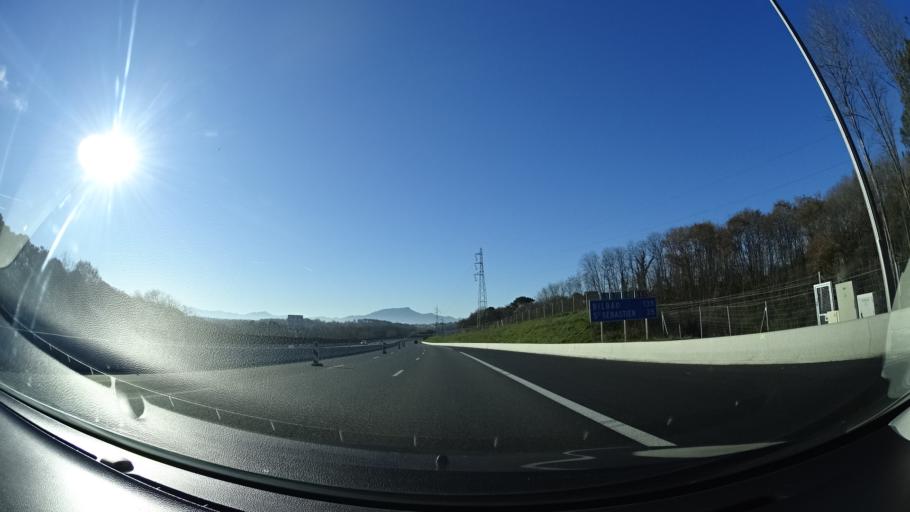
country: FR
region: Aquitaine
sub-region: Departement des Pyrenees-Atlantiques
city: Arbonne
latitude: 43.4445
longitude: -1.5655
